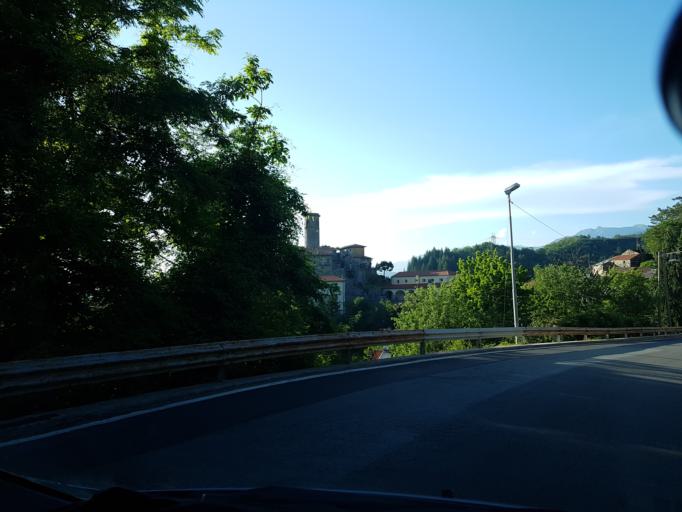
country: IT
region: Tuscany
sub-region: Provincia di Lucca
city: Minucciano
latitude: 44.1687
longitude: 10.2087
